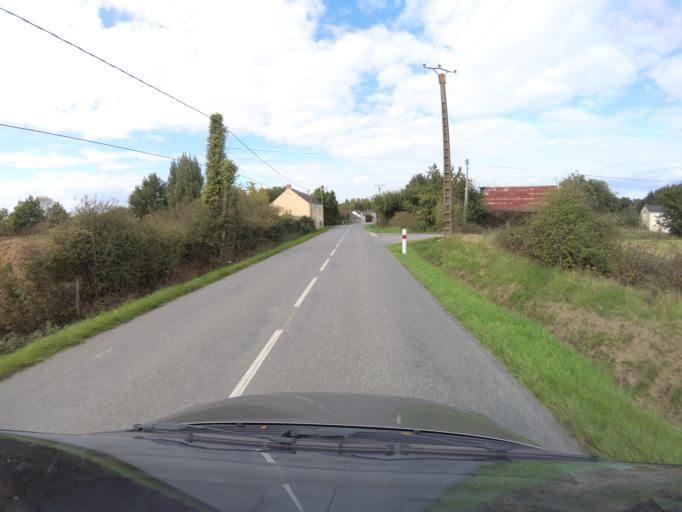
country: FR
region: Pays de la Loire
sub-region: Departement de la Loire-Atlantique
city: Bouvron
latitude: 47.4707
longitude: -1.8384
